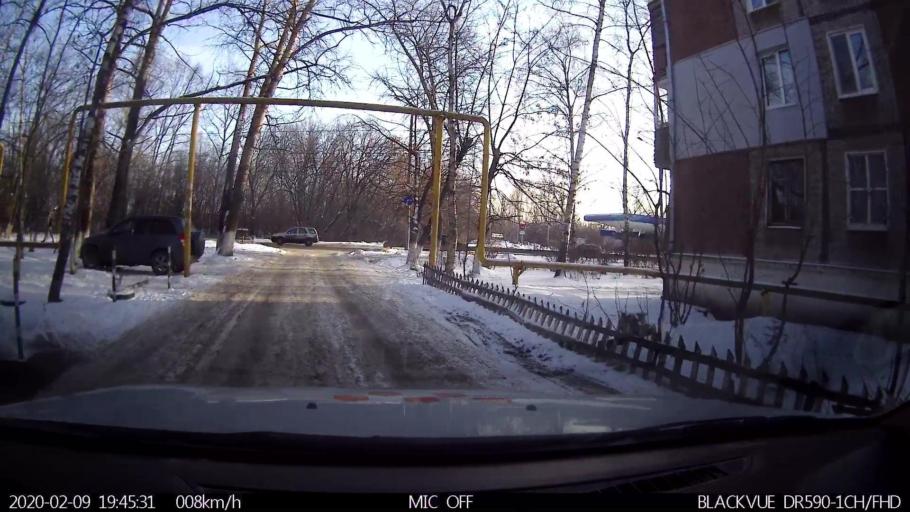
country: RU
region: Nizjnij Novgorod
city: Gorbatovka
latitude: 56.3382
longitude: 43.8467
